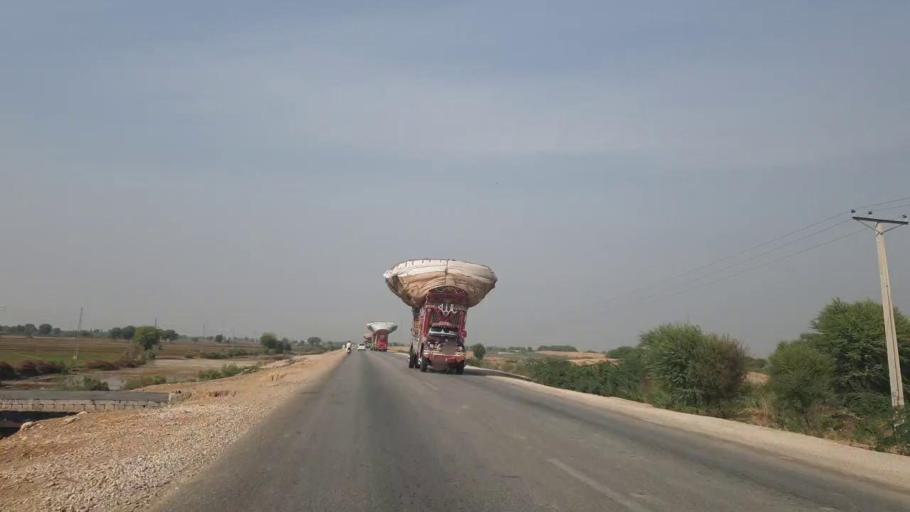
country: PK
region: Sindh
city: Sann
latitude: 26.0695
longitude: 68.0997
